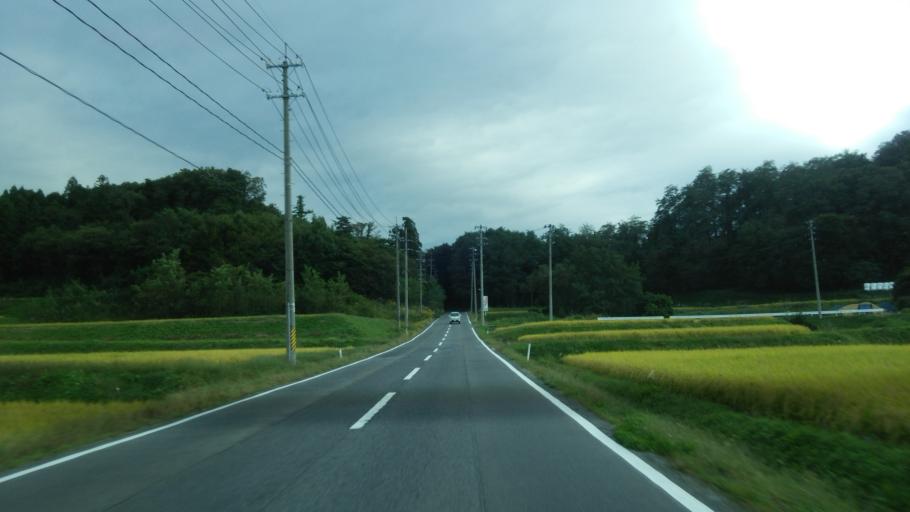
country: JP
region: Fukushima
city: Sukagawa
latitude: 37.2874
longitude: 140.2743
